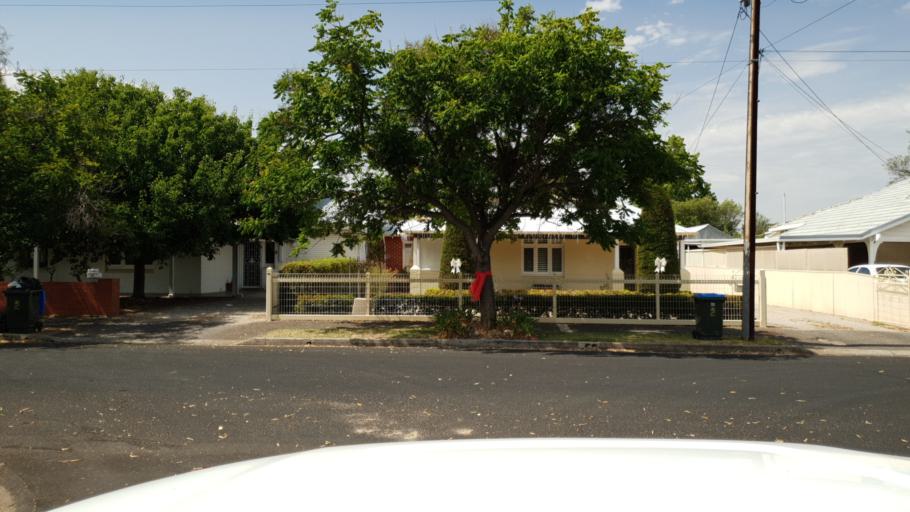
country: AU
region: South Australia
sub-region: Mitcham
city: Clarence Gardens
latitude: -34.9732
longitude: 138.5864
